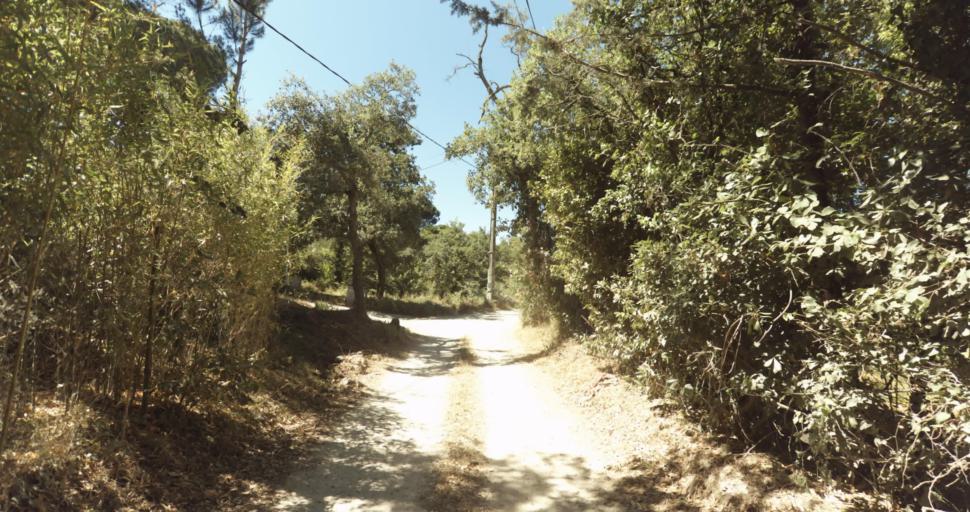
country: FR
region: Provence-Alpes-Cote d'Azur
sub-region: Departement du Var
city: Gassin
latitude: 43.2378
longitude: 6.5670
